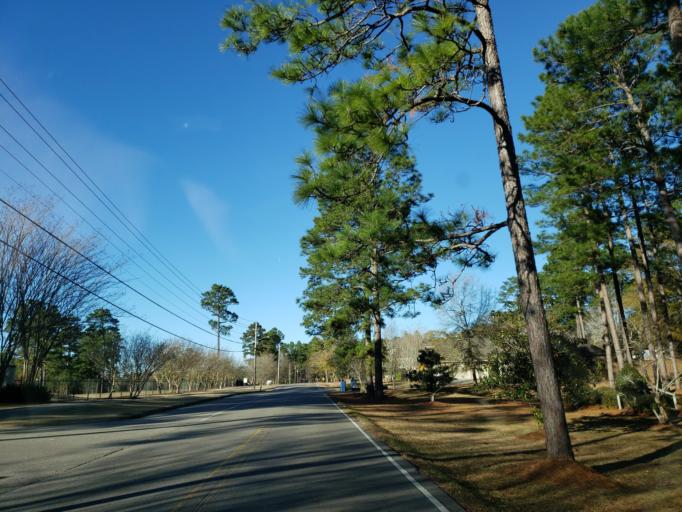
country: US
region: Mississippi
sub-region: Lamar County
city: Arnold Line
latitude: 31.3510
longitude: -89.3776
